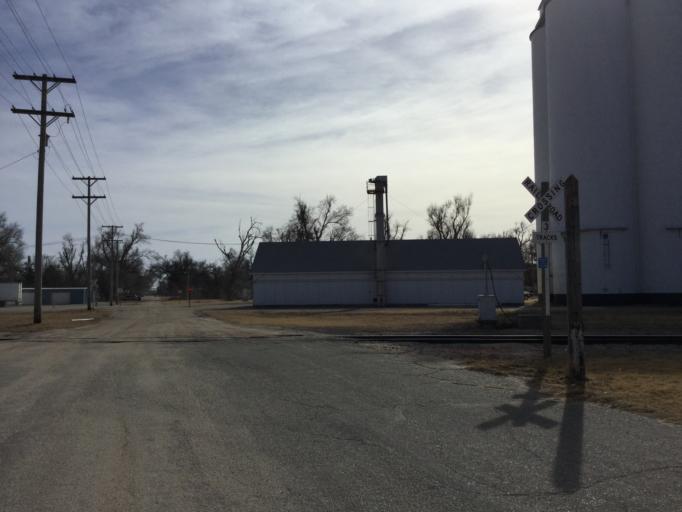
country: US
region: Kansas
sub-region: Rice County
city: Sterling
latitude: 38.2078
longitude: -98.2083
